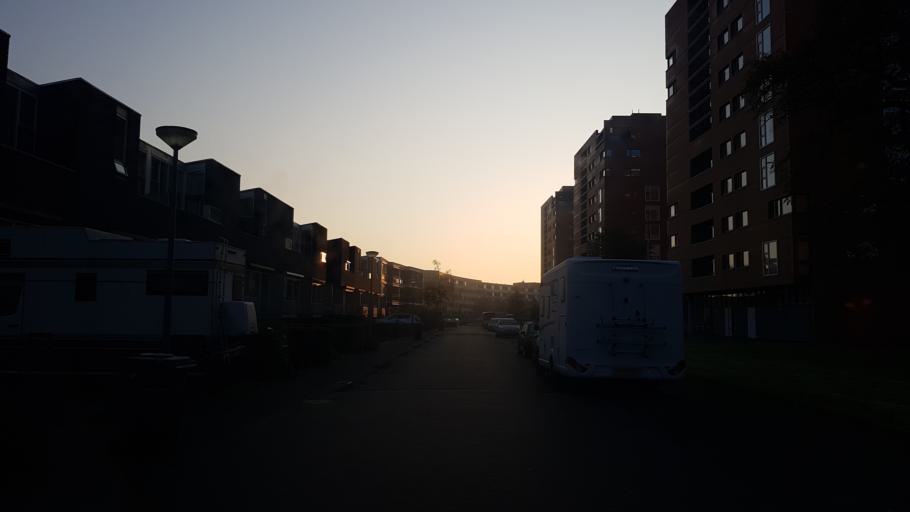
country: NL
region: Gelderland
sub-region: Gemeente Apeldoorn
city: Apeldoorn
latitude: 52.2139
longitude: 5.9722
